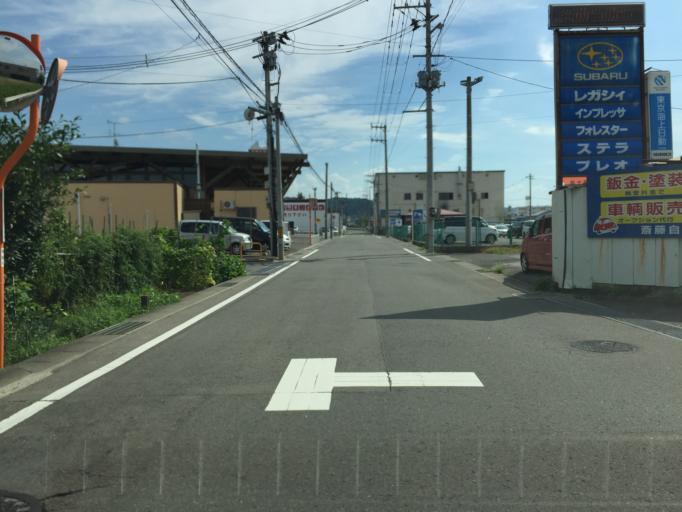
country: JP
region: Fukushima
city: Fukushima-shi
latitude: 37.7323
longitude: 140.4652
